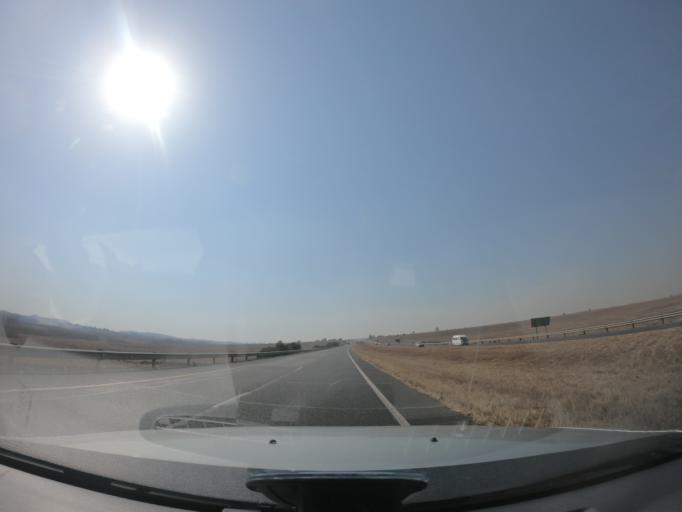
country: ZA
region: Mpumalanga
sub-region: Nkangala District Municipality
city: Middelburg
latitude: -25.8491
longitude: 29.3923
